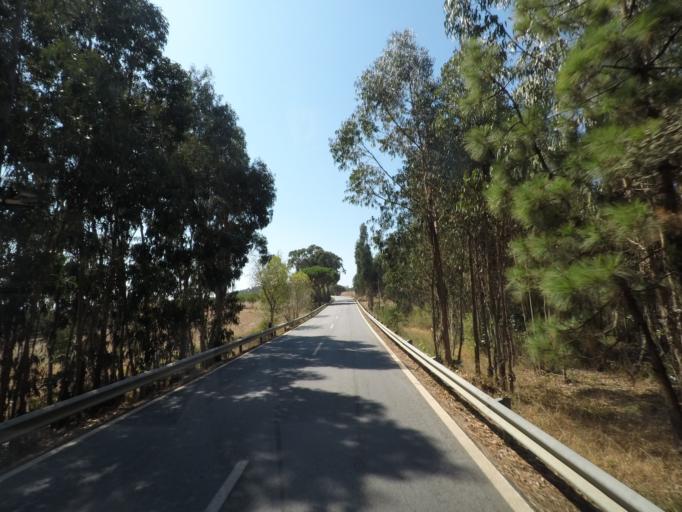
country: PT
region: Beja
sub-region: Odemira
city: Sao Teotonio
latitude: 37.5388
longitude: -8.6904
